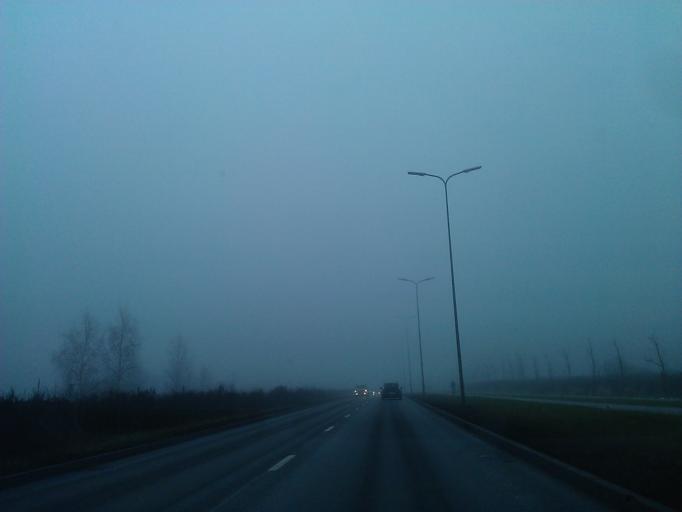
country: LV
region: Stopini
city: Ulbroka
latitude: 56.9537
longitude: 24.2515
